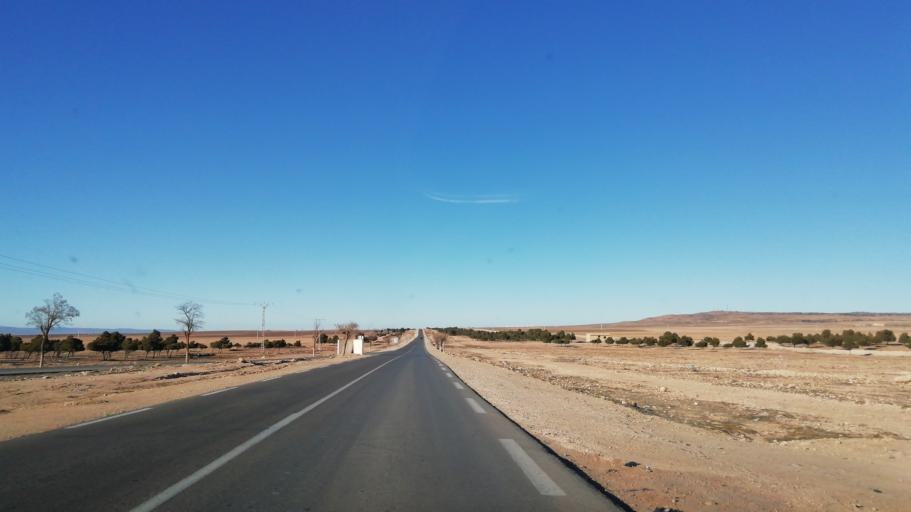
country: DZ
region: Tlemcen
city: Sebdou
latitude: 34.2330
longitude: -1.2564
